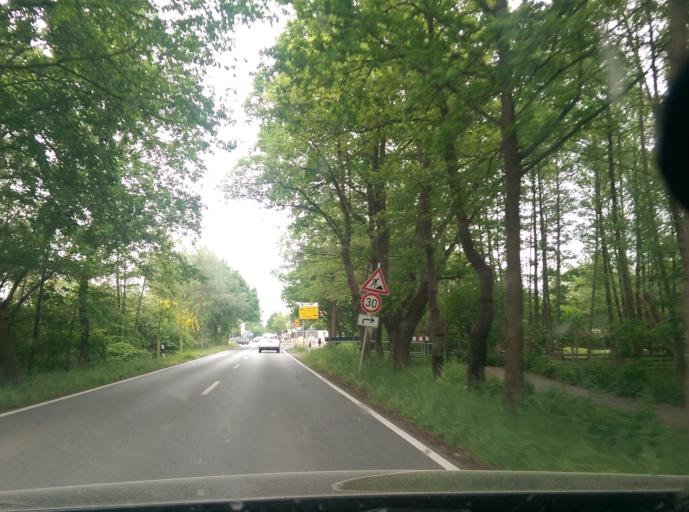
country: DE
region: Lower Saxony
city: Garbsen-Mitte
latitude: 52.4481
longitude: 9.6071
